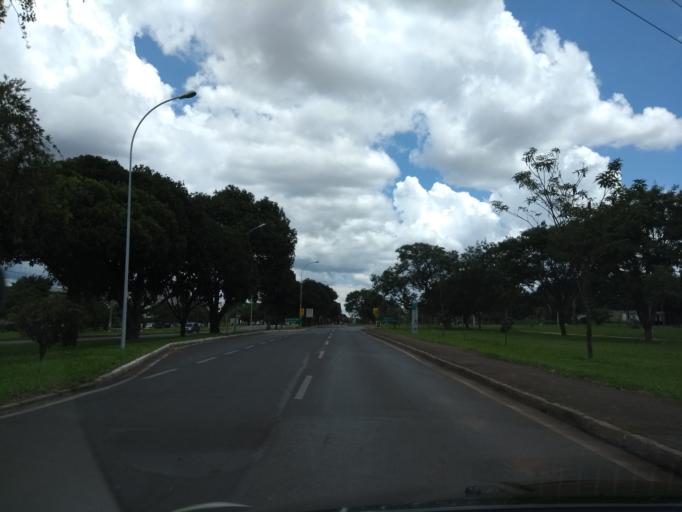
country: BR
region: Federal District
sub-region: Brasilia
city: Brasilia
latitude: -15.7979
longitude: -47.9334
